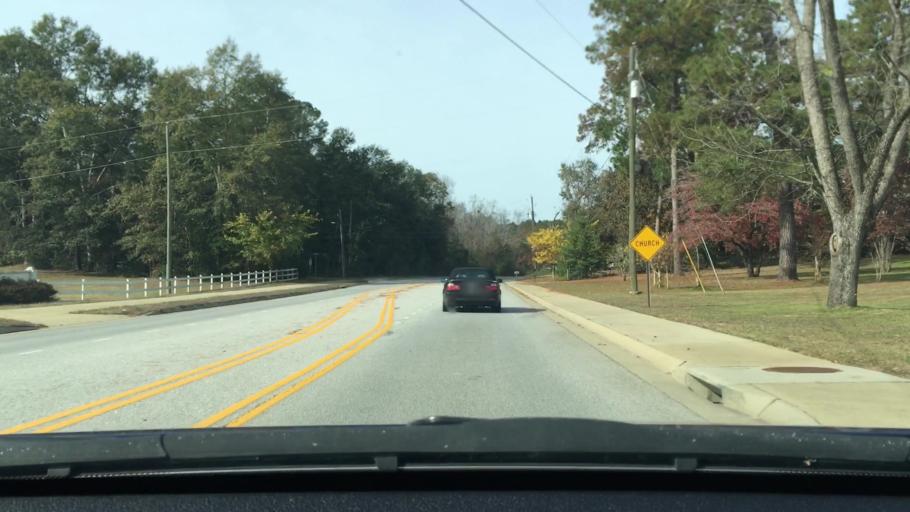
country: US
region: South Carolina
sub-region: Sumter County
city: South Sumter
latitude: 33.9164
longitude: -80.3903
